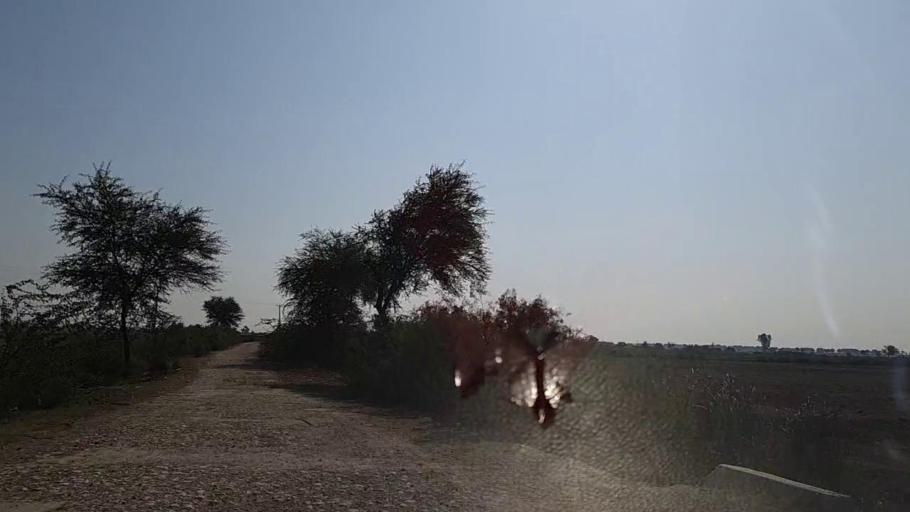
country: PK
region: Sindh
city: Sanghar
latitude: 25.9878
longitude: 69.0610
